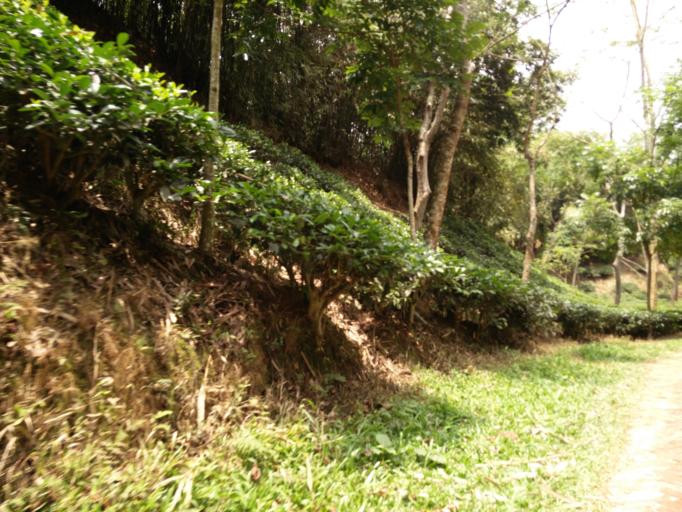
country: IN
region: Tripura
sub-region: Dhalai
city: Kamalpur
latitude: 24.3035
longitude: 91.8002
